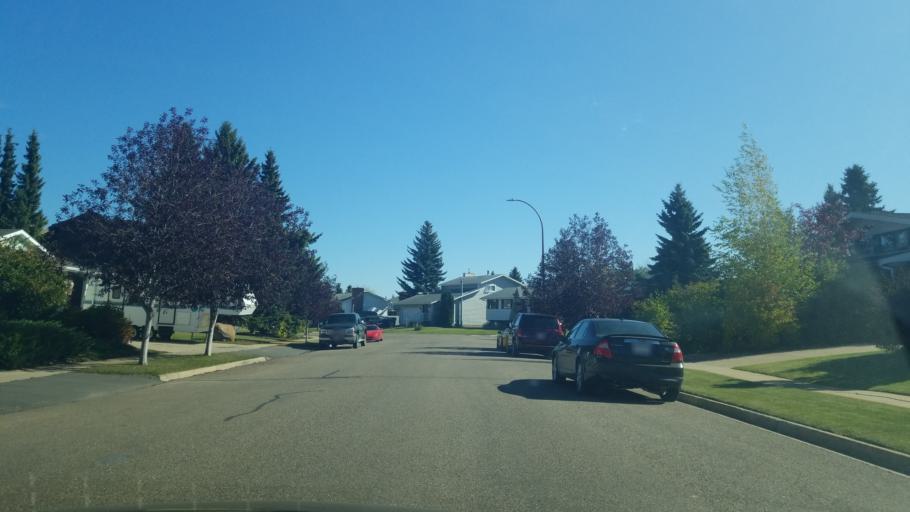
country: CA
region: Saskatchewan
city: Lloydminster
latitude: 53.2713
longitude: -110.0164
